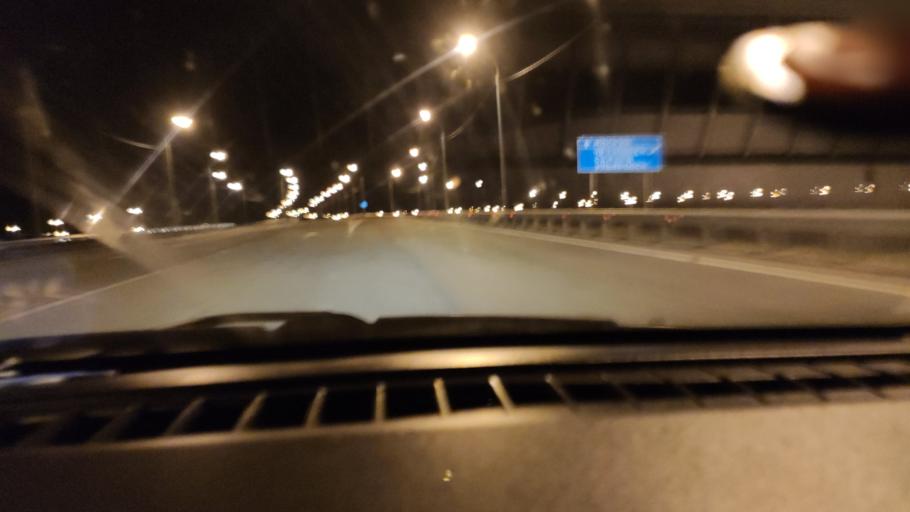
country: RU
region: Samara
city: Varlamovo
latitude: 53.1954
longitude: 48.2948
